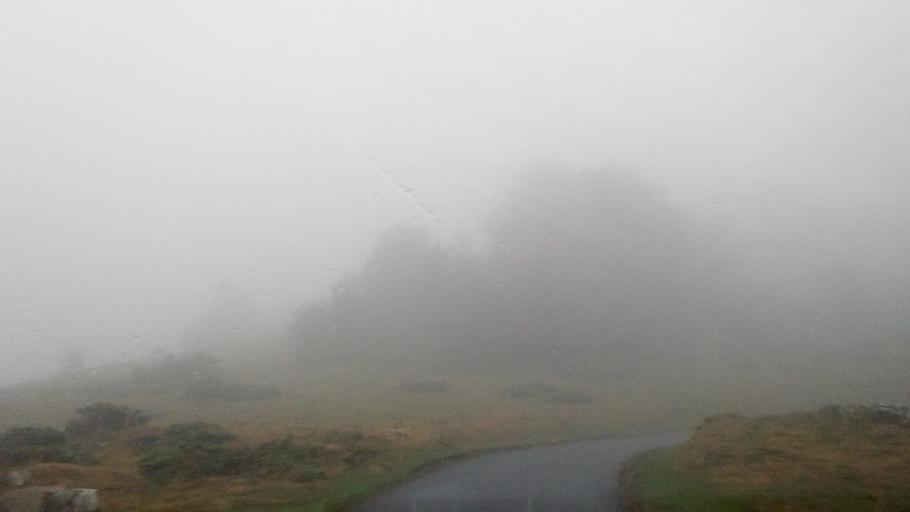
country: FR
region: Midi-Pyrenees
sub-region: Departement des Hautes-Pyrenees
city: Saint-Lary-Soulan
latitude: 42.9106
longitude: 0.2978
